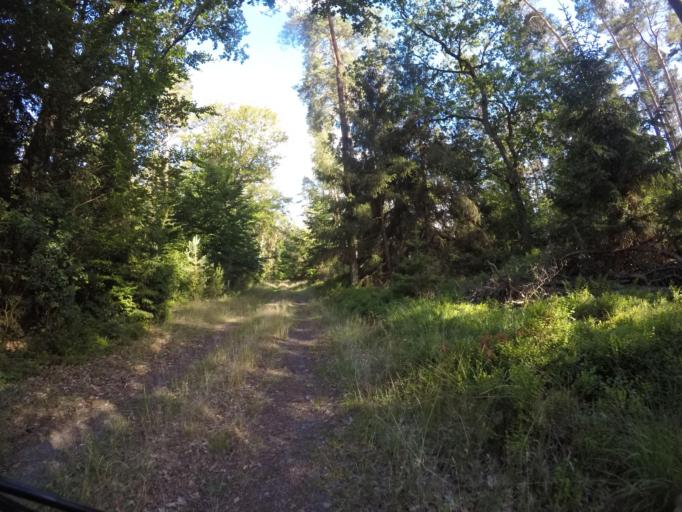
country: DE
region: Mecklenburg-Vorpommern
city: Lubtheen
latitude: 53.2386
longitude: 11.0236
